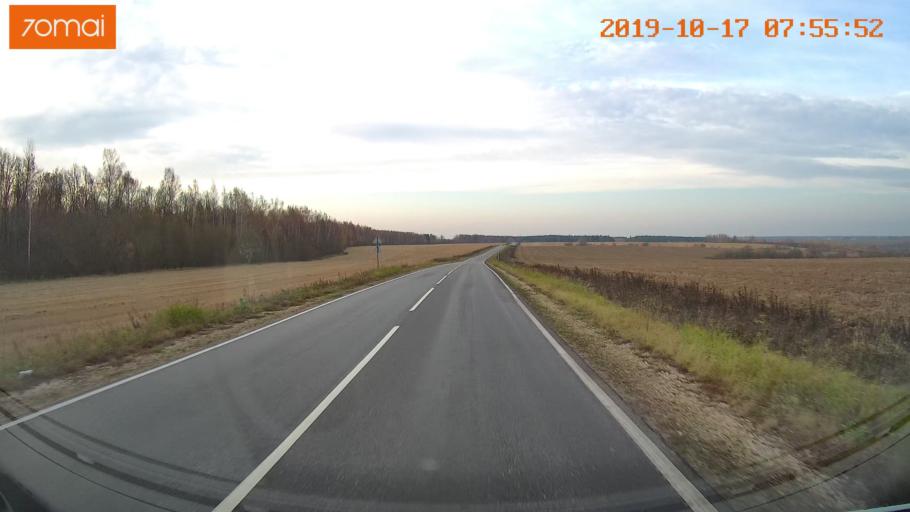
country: RU
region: Vladimir
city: Bavleny
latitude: 56.4303
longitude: 39.5972
